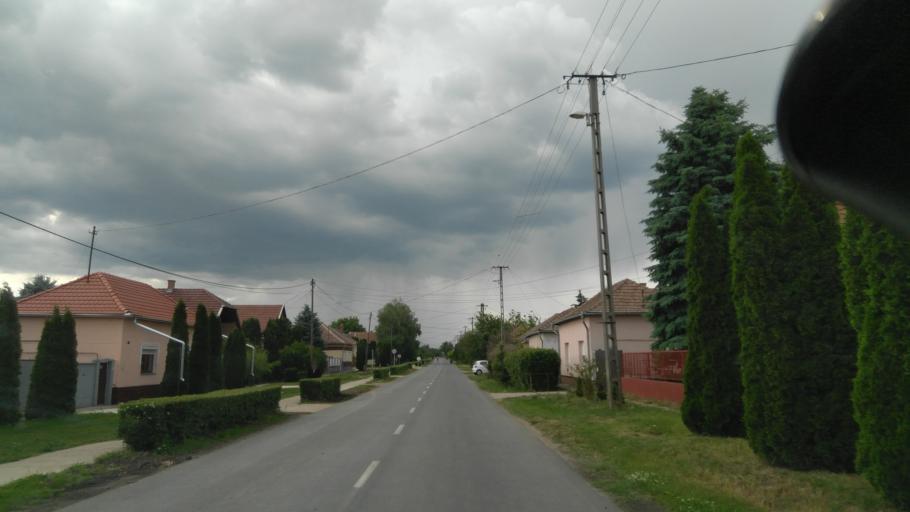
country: HU
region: Bekes
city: Dombegyhaz
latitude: 46.3424
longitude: 21.1282
